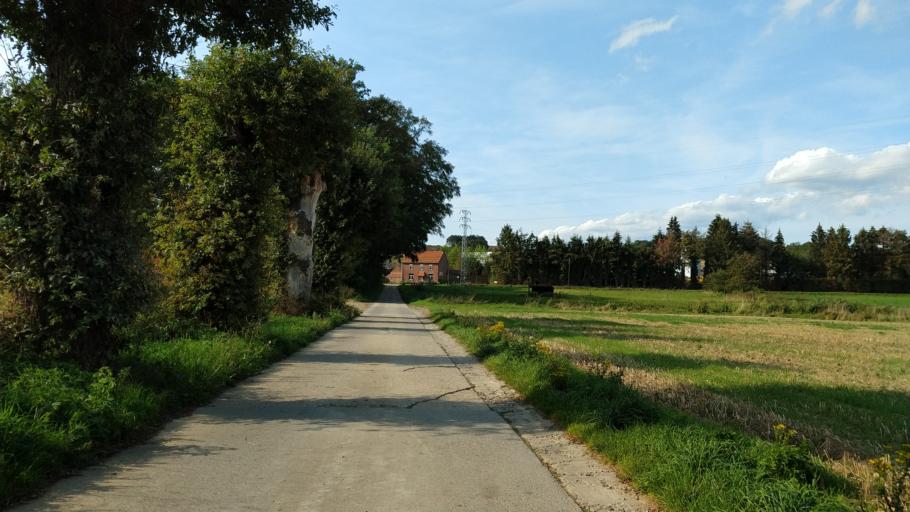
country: BE
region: Flanders
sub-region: Provincie Vlaams-Brabant
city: Lubbeek
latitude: 50.8636
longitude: 4.8194
